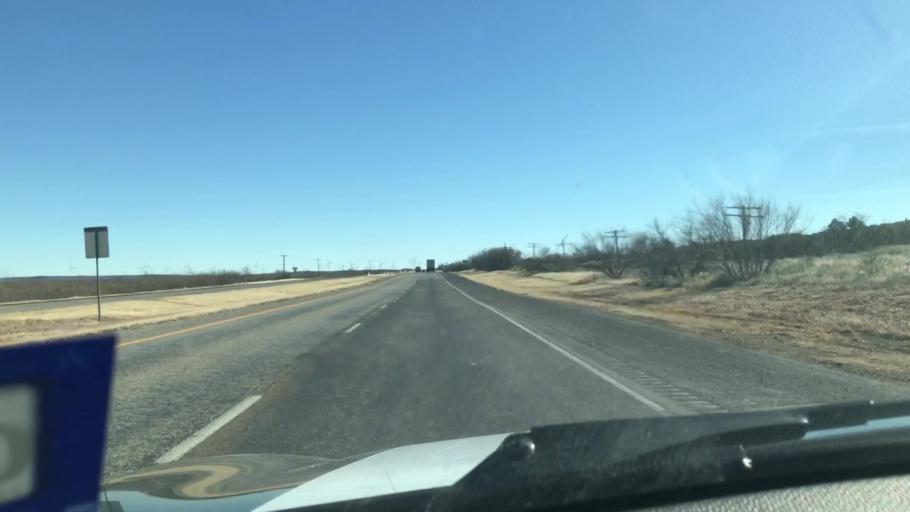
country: US
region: Texas
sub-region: Scurry County
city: Snyder
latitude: 32.9628
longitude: -101.0930
